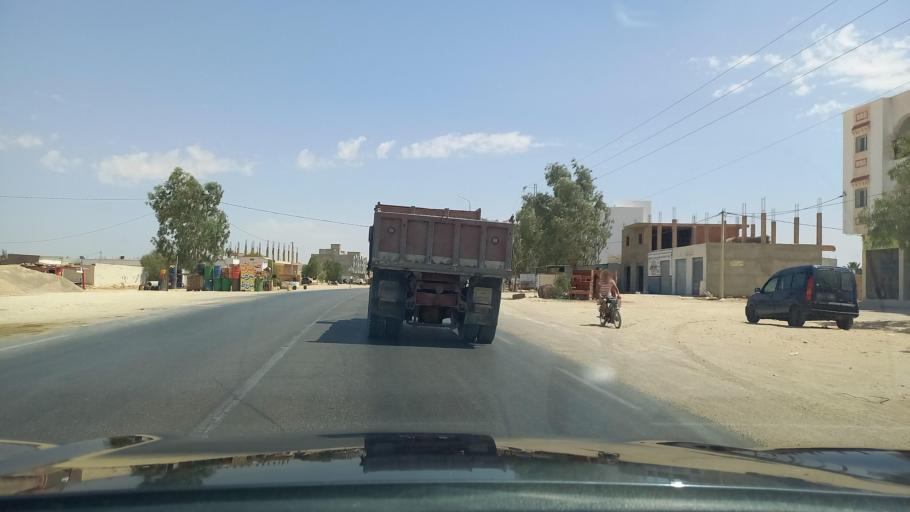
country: TN
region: Madanin
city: Medenine
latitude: 33.3669
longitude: 10.4557
